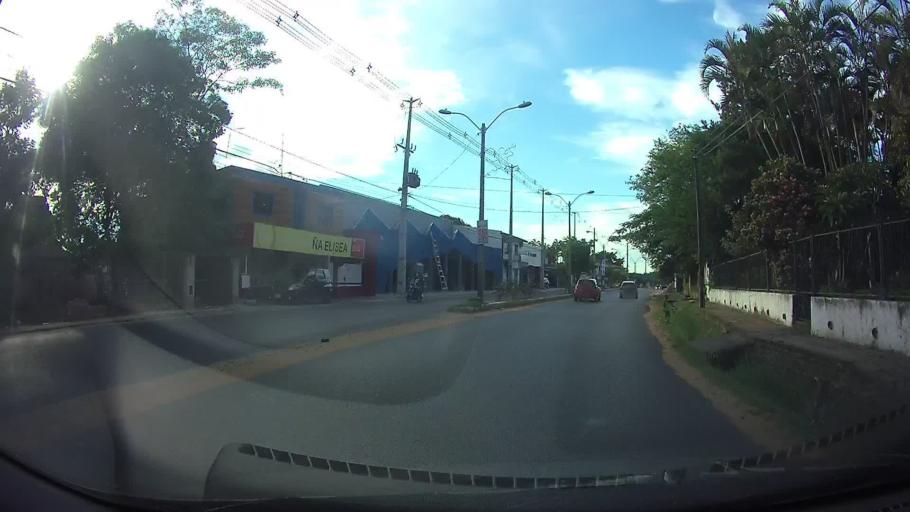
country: PY
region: Central
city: San Antonio
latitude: -25.4186
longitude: -57.5710
